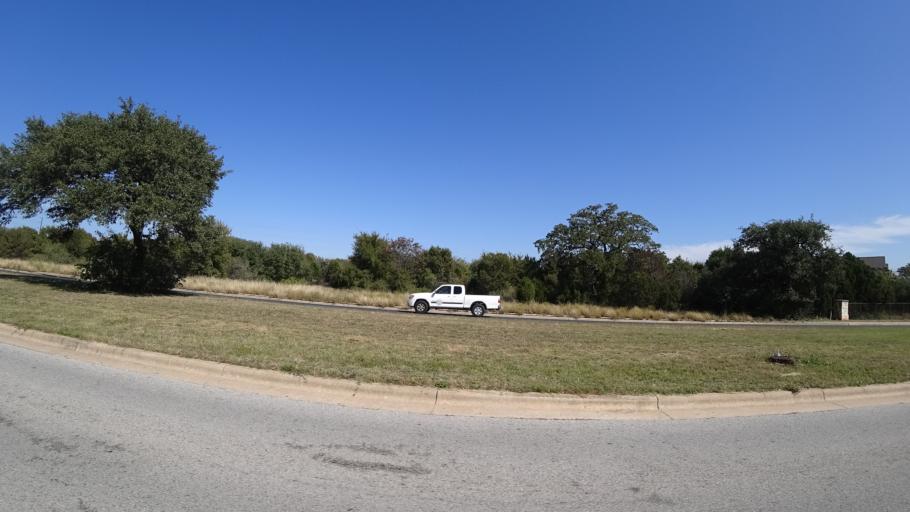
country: US
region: Texas
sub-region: Travis County
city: Shady Hollow
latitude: 30.1913
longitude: -97.8578
